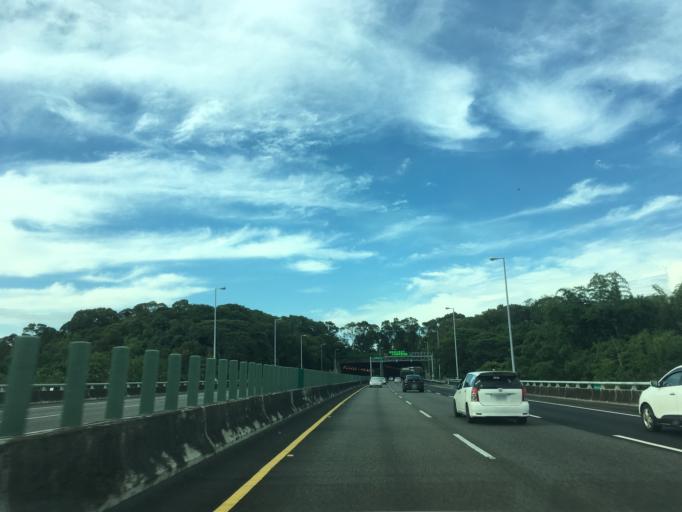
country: TW
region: Taiwan
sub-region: Chiayi
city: Jiayi Shi
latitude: 23.5741
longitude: 120.5067
